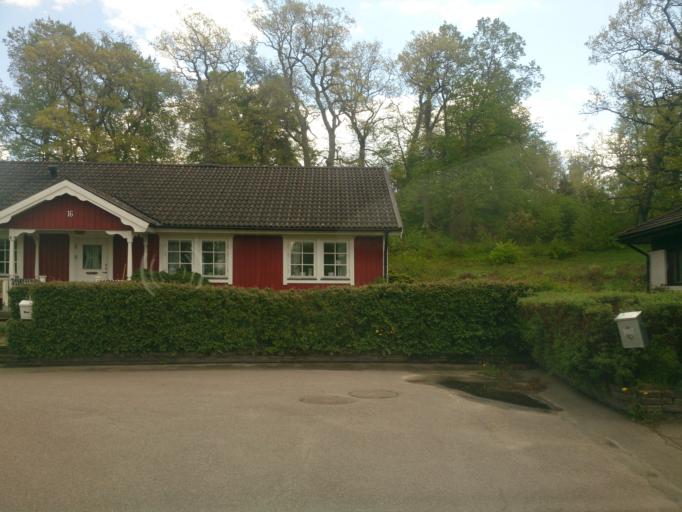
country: SE
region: OEstergoetland
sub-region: Atvidabergs Kommun
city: Atvidaberg
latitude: 58.2019
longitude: 15.9735
